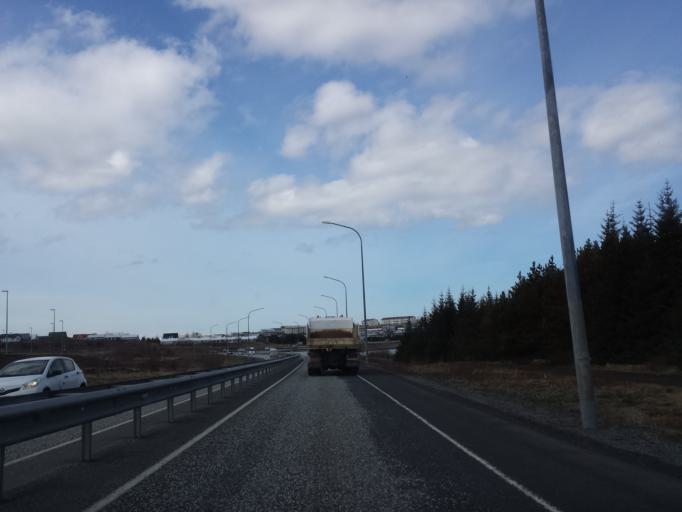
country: IS
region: Capital Region
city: Mosfellsbaer
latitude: 64.1038
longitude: -21.7687
